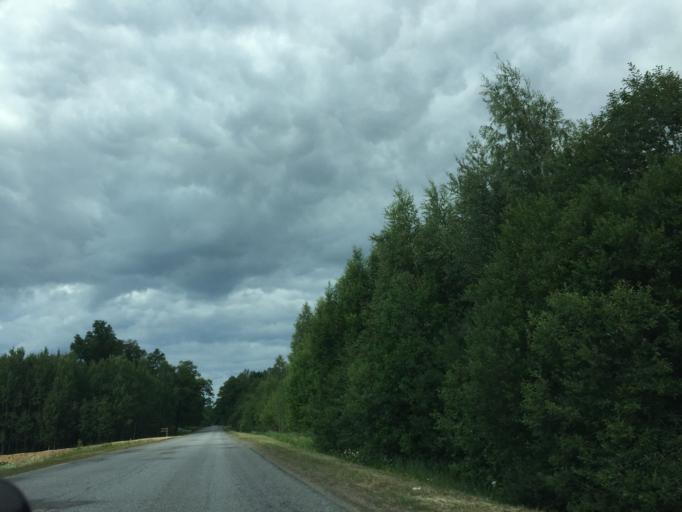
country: LV
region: Skriveri
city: Skriveri
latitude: 56.8273
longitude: 25.1255
